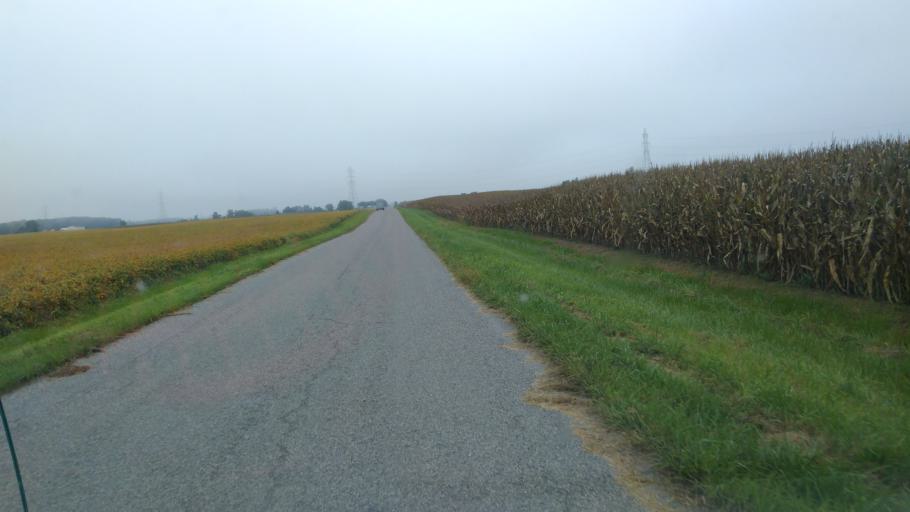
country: US
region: Ohio
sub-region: Logan County
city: Northwood
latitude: 40.4964
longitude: -83.5971
